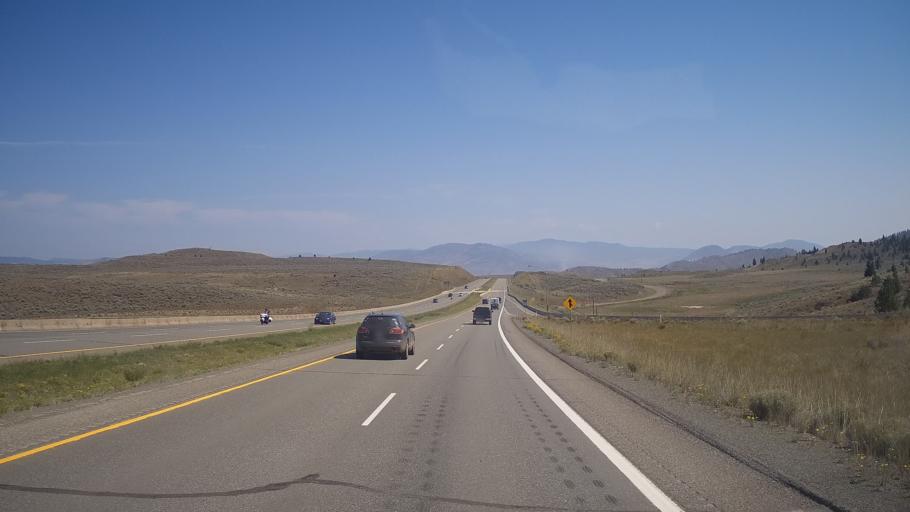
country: CA
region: British Columbia
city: Kamloops
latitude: 50.6537
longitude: -120.4812
